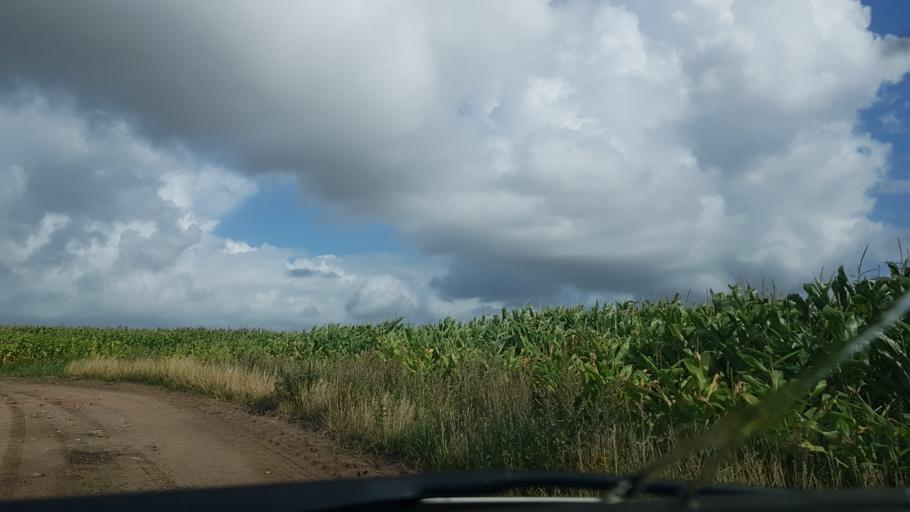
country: DK
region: South Denmark
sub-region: Esbjerg Kommune
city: Ribe
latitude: 55.2580
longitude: 8.7611
